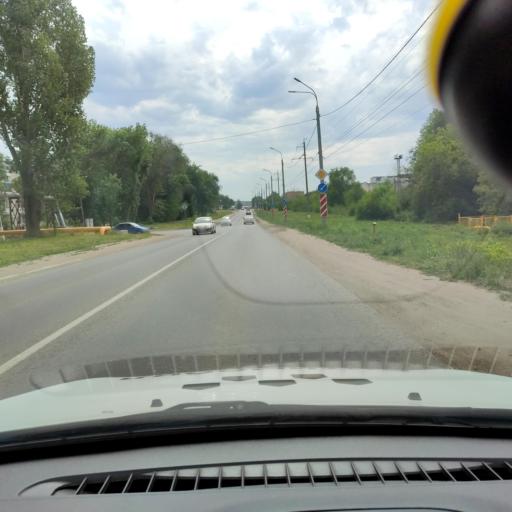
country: RU
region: Samara
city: Zhigulevsk
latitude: 53.4085
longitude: 49.5239
